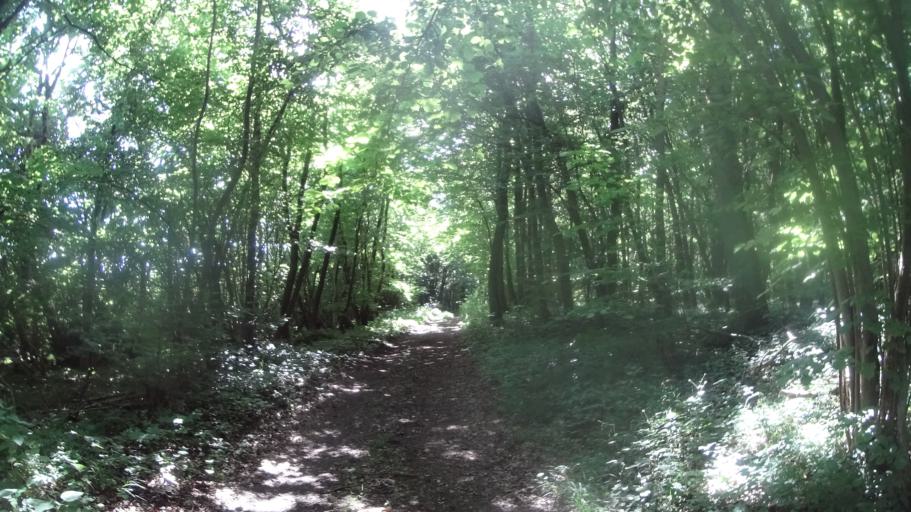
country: DE
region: Lower Saxony
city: Elbe
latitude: 52.1060
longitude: 10.3145
